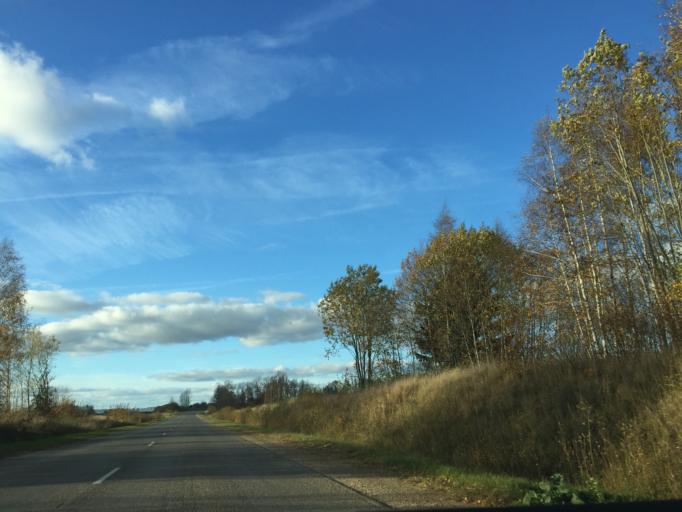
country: LV
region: Tukuma Rajons
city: Tukums
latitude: 56.9841
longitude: 23.1079
